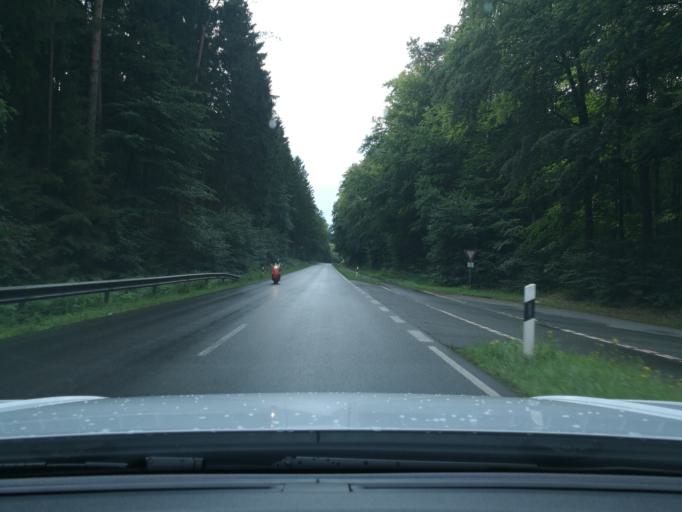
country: DE
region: Schleswig-Holstein
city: Aumuhle
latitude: 53.5180
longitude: 10.3502
